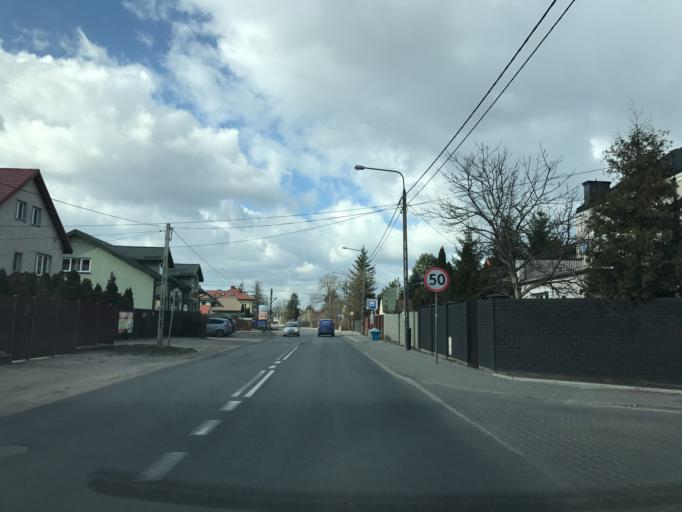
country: PL
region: Masovian Voivodeship
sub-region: Warszawa
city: Rembertow
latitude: 52.2663
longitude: 21.1548
